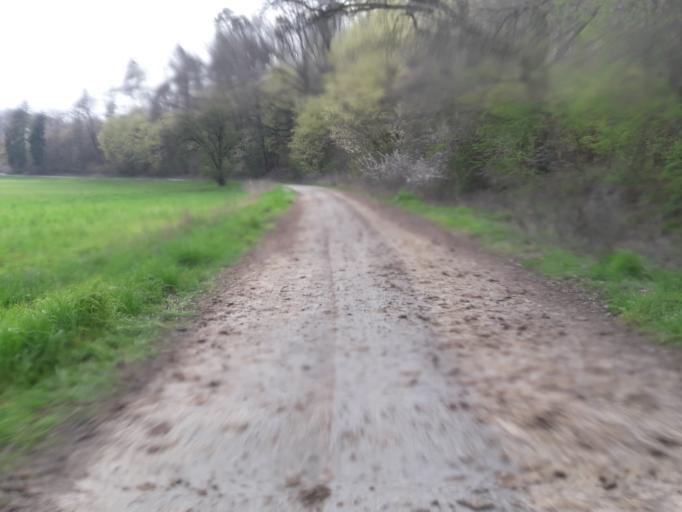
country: DE
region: North Rhine-Westphalia
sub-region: Regierungsbezirk Detmold
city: Paderborn
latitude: 51.6734
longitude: 8.7804
